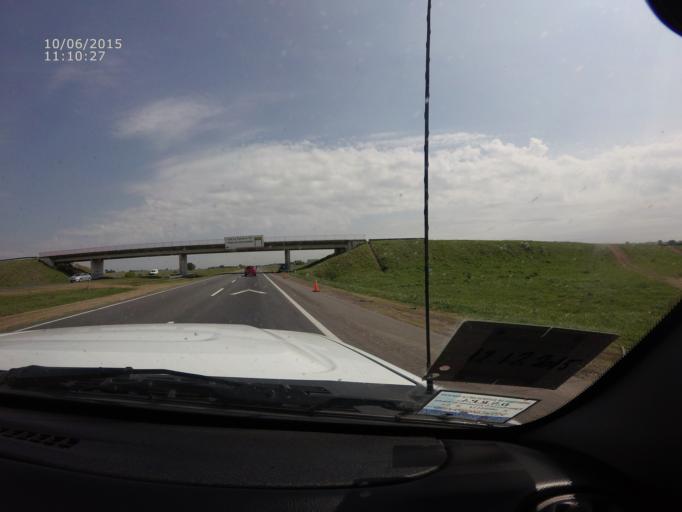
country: AR
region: Santa Fe
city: Arroyo Seco
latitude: -33.1521
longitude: -60.5496
